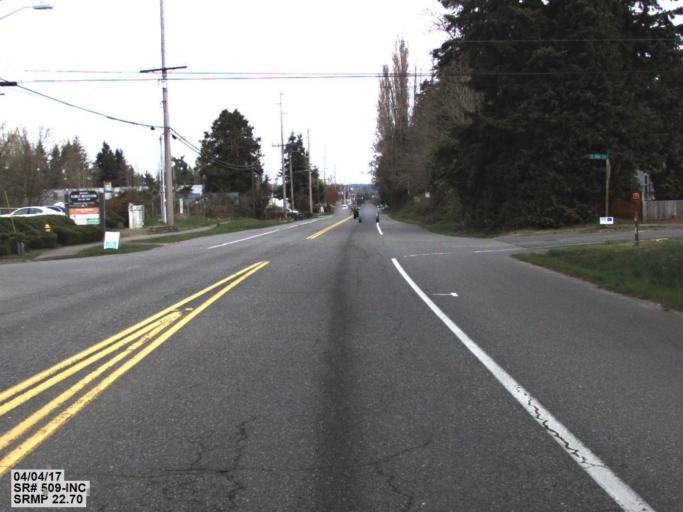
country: US
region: Washington
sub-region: King County
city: Normandy Park
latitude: 47.4363
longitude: -122.3351
